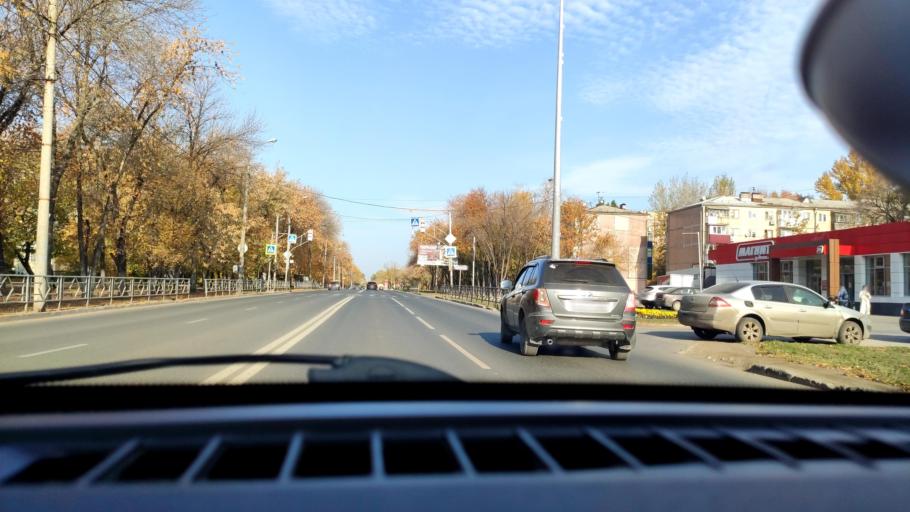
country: RU
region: Samara
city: Samara
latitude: 53.2179
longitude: 50.2076
